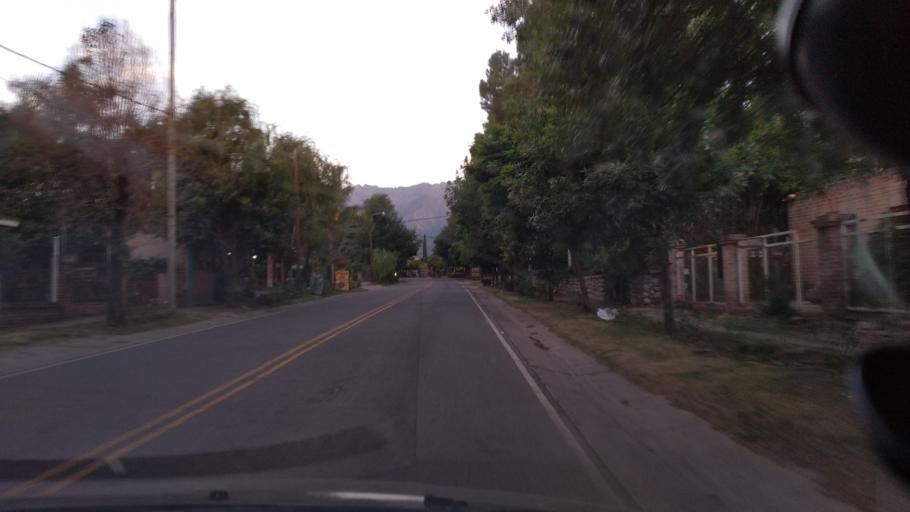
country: AR
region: Cordoba
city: Villa Las Rosas
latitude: -31.9521
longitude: -65.0577
